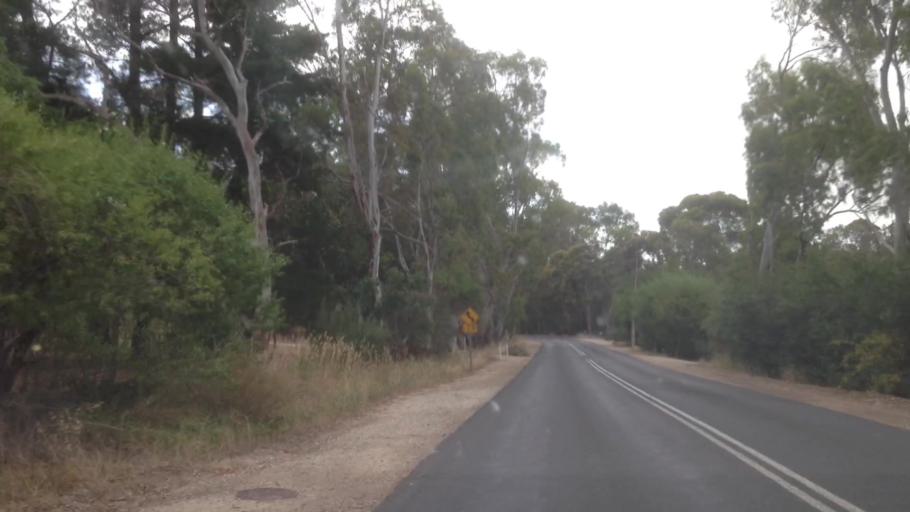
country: AU
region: South Australia
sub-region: Barossa
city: Williamstown
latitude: -34.6625
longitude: 138.8684
